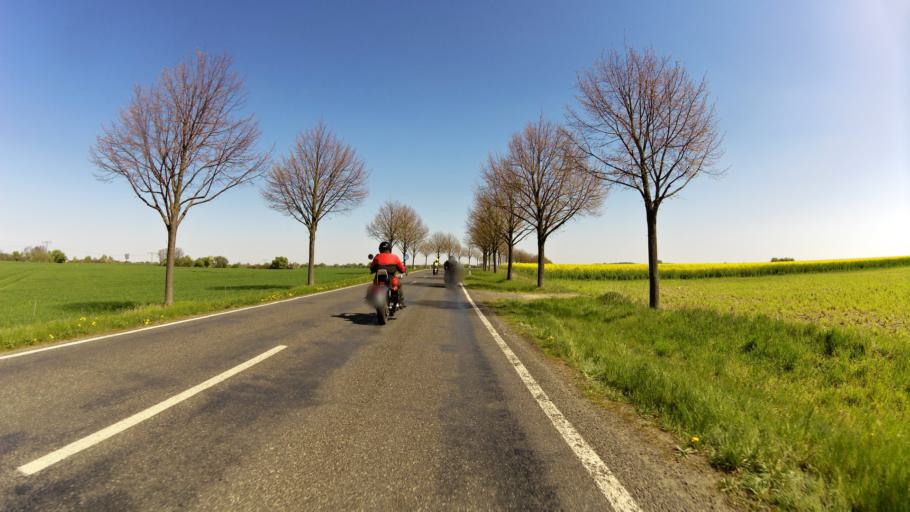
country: DE
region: Brandenburg
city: Waldsieversdorf
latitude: 52.5762
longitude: 14.0091
